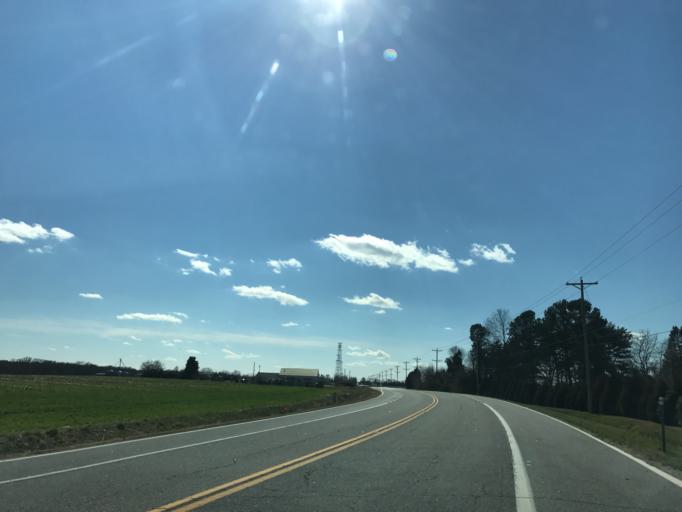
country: US
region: Maryland
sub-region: Kent County
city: Chestertown
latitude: 39.2214
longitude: -76.1656
